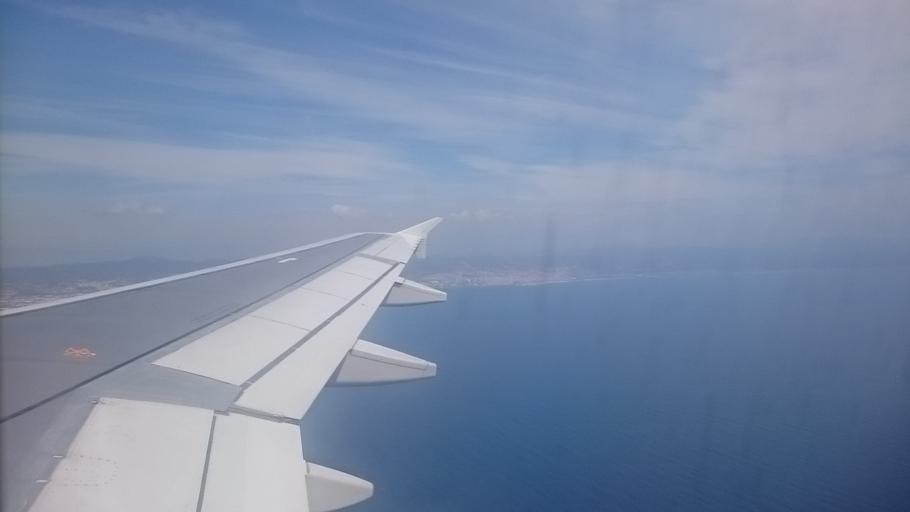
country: ES
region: Catalonia
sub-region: Provincia de Barcelona
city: Vilassar de Mar
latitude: 41.4239
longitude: 2.4514
